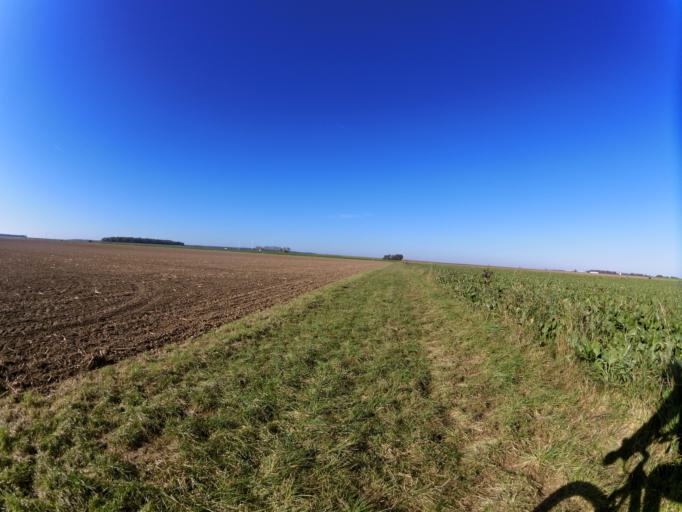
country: DE
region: Bavaria
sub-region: Regierungsbezirk Unterfranken
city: Giebelstadt
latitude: 49.6638
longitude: 9.9374
